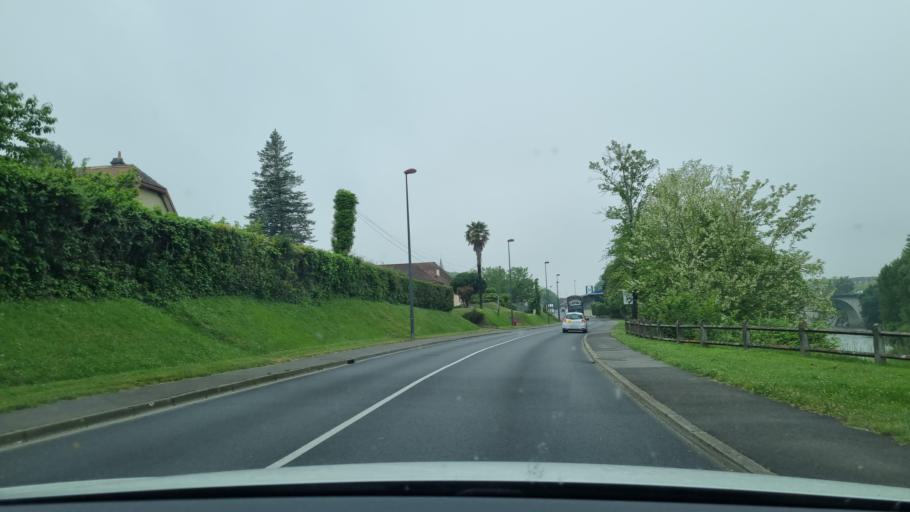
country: FR
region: Aquitaine
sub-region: Departement des Pyrenees-Atlantiques
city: Orthez
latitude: 43.4828
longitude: -0.7714
